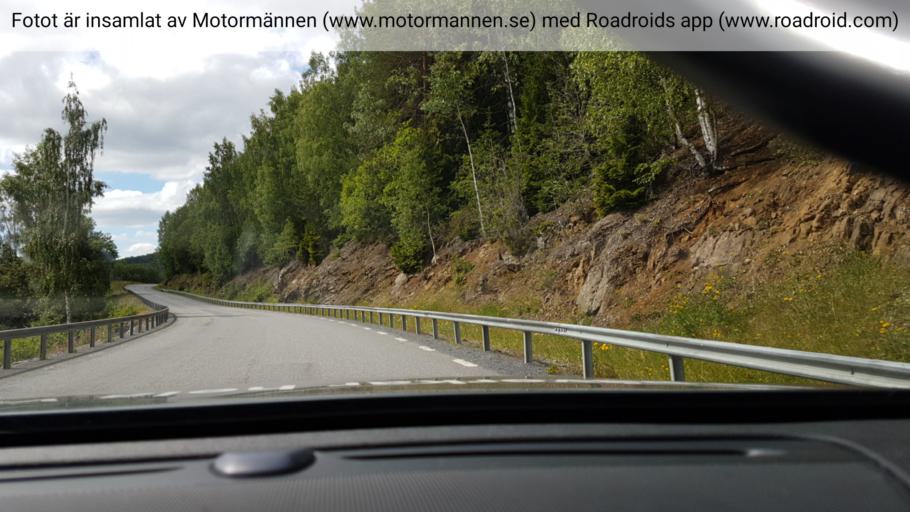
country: SE
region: Vaesternorrland
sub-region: Kramfors Kommun
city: Nordingra
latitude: 62.9418
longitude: 18.2467
